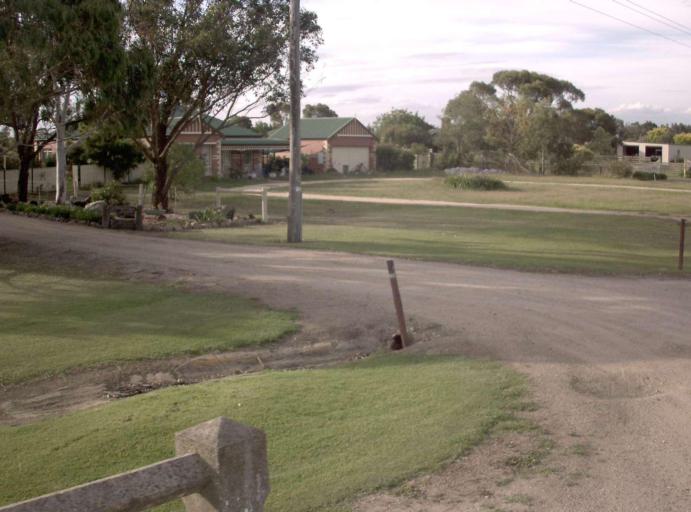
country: AU
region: Victoria
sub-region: Wellington
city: Sale
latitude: -37.9533
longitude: 146.9875
